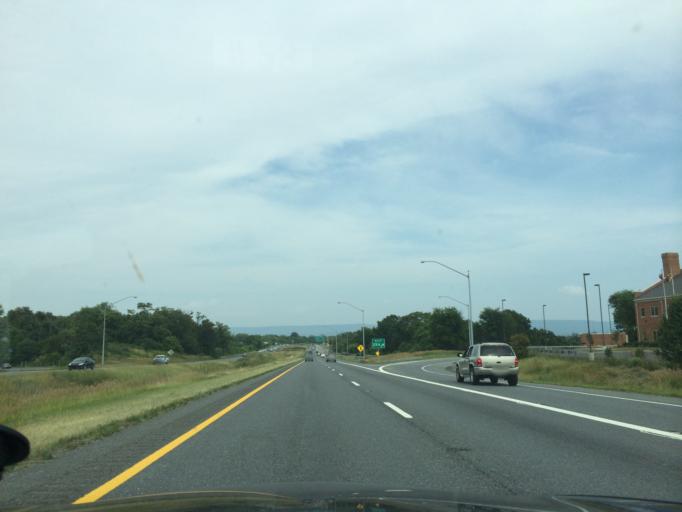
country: US
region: Maryland
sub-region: Washington County
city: Halfway
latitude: 39.6052
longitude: -77.7343
